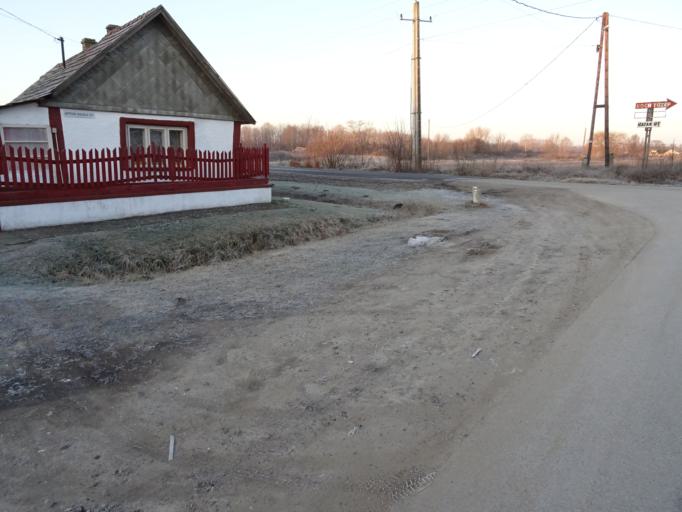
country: HU
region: Pest
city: Nagykata
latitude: 47.4219
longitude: 19.7185
